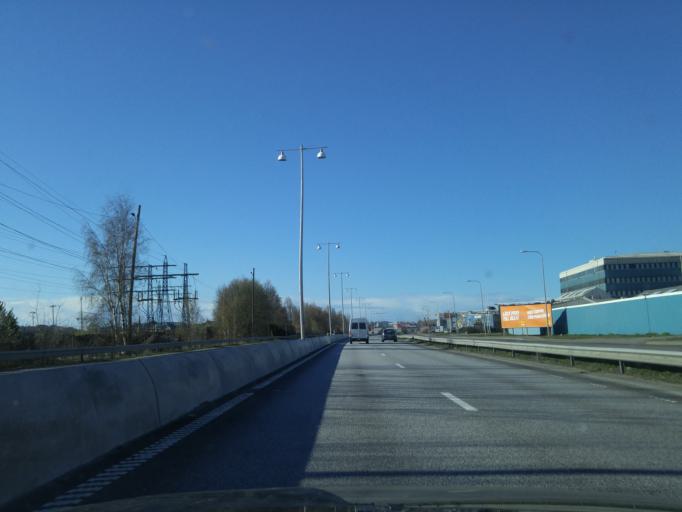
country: SE
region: Vaestra Goetaland
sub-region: Goteborg
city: Goeteborg
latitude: 57.7358
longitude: 12.0026
